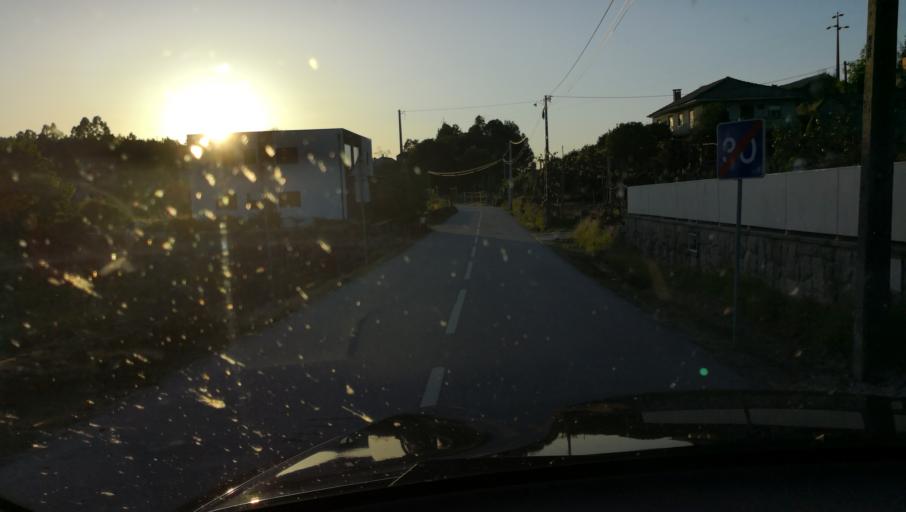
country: PT
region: Vila Real
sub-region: Mondim de Basto
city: Mondim de Basto
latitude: 41.4085
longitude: -7.9279
